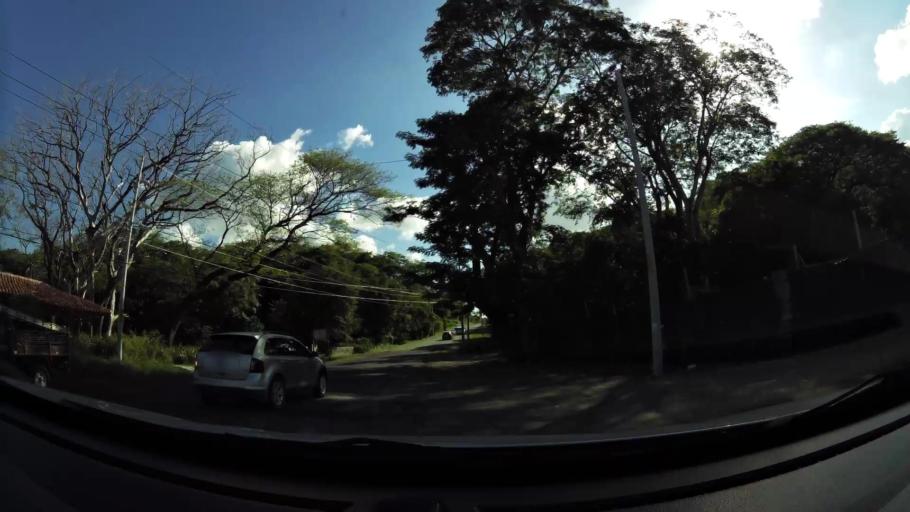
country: CR
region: Guanacaste
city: Sardinal
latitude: 10.5865
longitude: -85.6600
